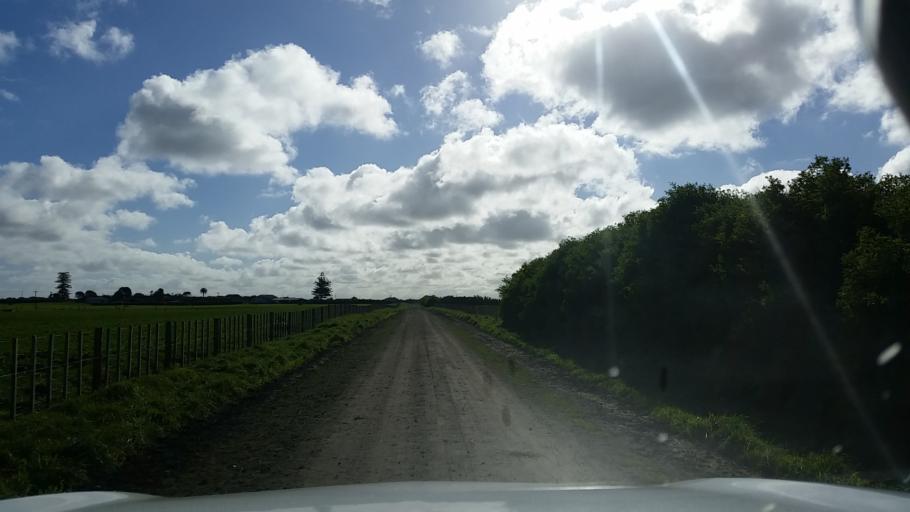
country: NZ
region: Taranaki
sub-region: South Taranaki District
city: Patea
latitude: -39.7524
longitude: 174.5207
